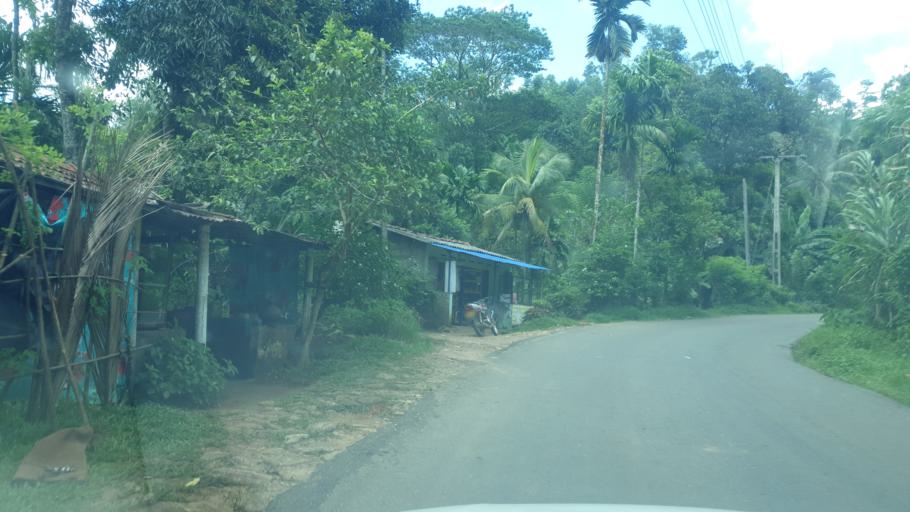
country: LK
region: Sabaragamuwa
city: Ratnapura
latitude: 6.4869
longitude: 80.4032
